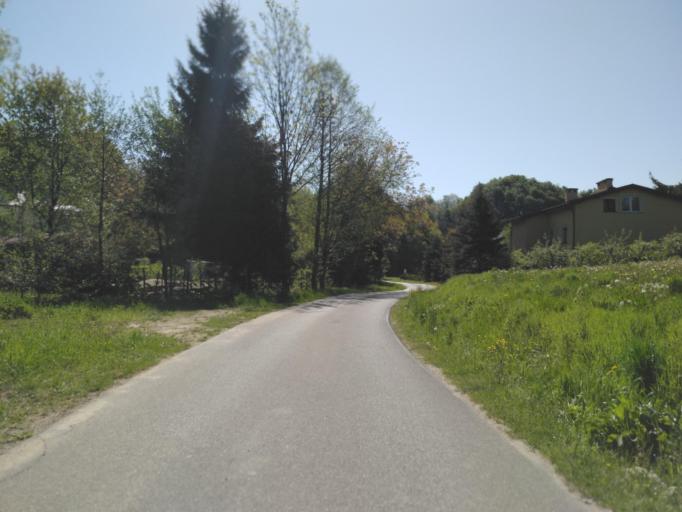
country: PL
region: Subcarpathian Voivodeship
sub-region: Powiat krosnienski
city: Korczyna
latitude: 49.7282
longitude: 21.8274
